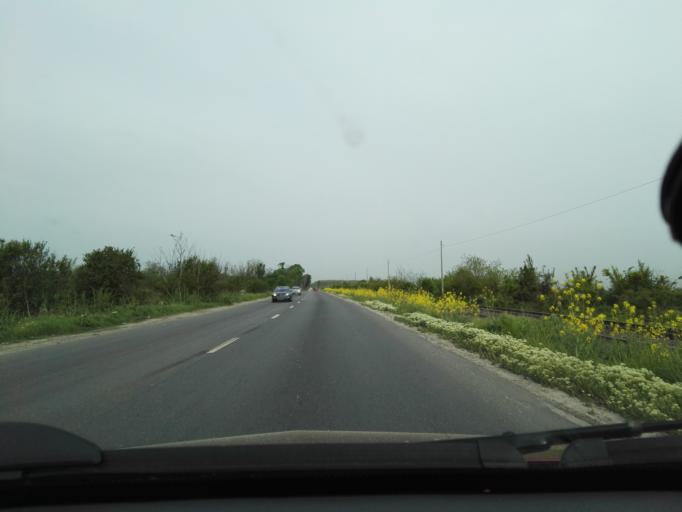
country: RO
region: Ilfov
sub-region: Comuna Jilava
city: Jilava
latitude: 44.3465
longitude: 26.0750
